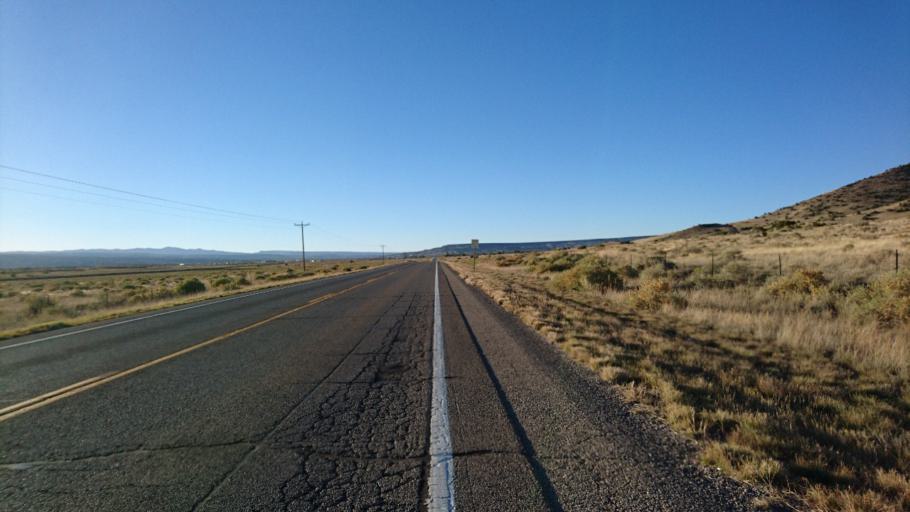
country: US
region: New Mexico
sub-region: Cibola County
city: Grants
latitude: 35.1167
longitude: -107.7883
